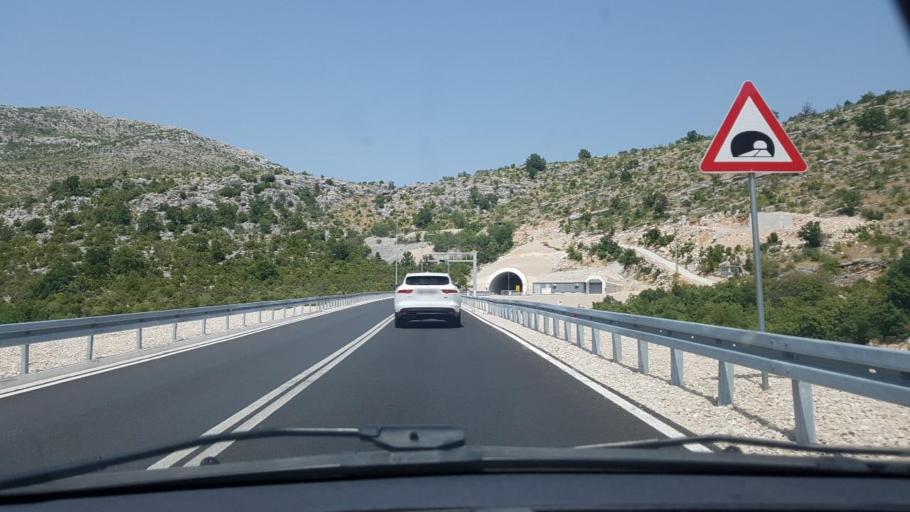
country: HR
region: Dubrovacko-Neretvanska
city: Podgora
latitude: 42.9520
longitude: 17.7849
